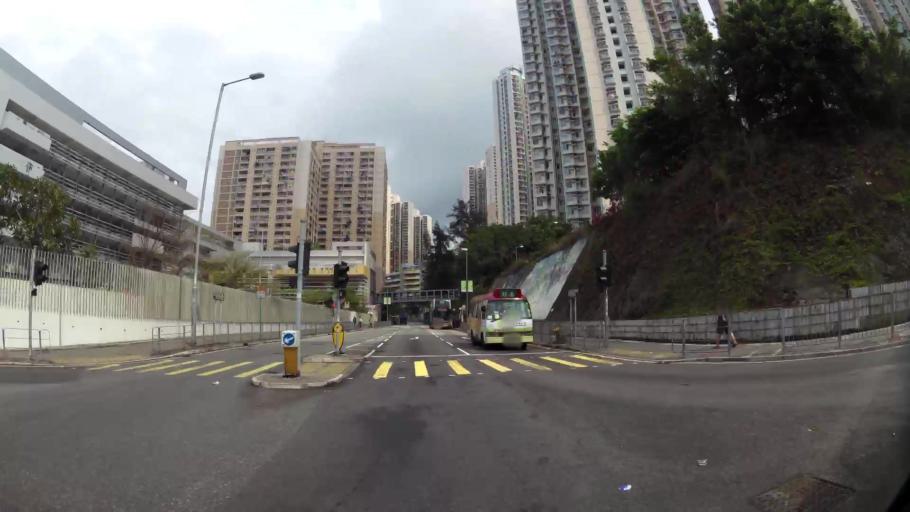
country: HK
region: Kowloon City
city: Kowloon
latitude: 22.3146
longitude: 114.2348
